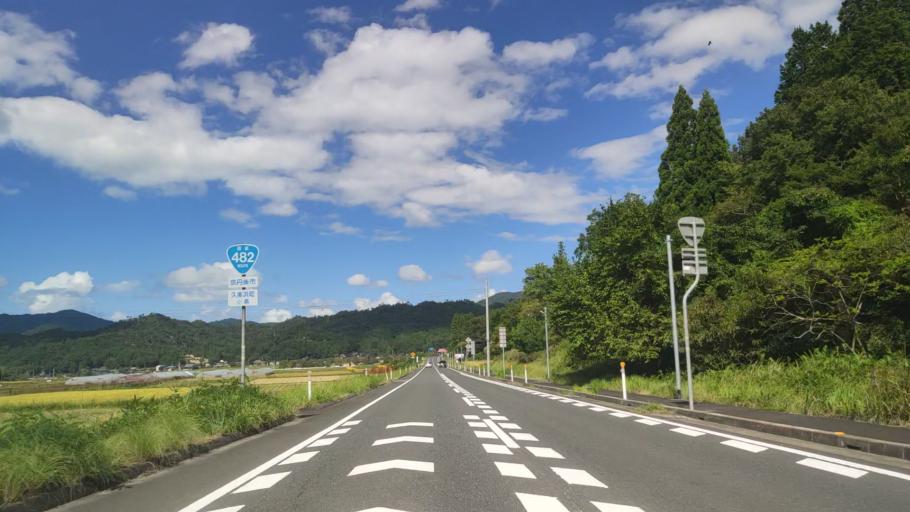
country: JP
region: Hyogo
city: Toyooka
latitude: 35.5670
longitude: 134.9739
